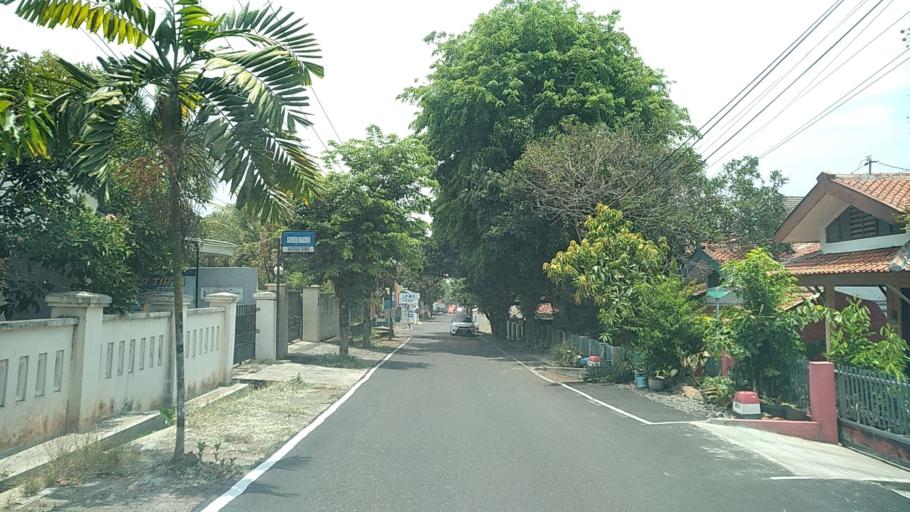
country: ID
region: Central Java
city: Semarang
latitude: -7.0496
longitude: 110.4116
